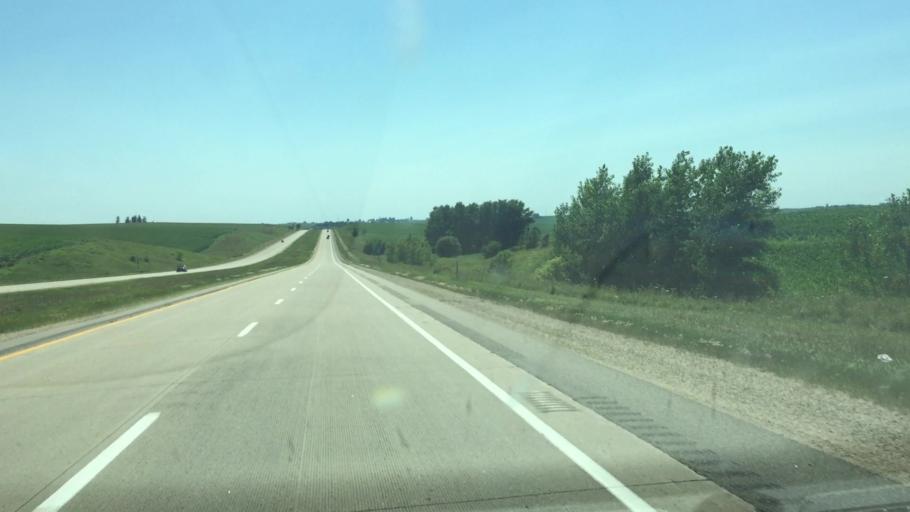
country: US
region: Iowa
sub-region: Dubuque County
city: Peosta
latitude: 42.3614
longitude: -90.8067
